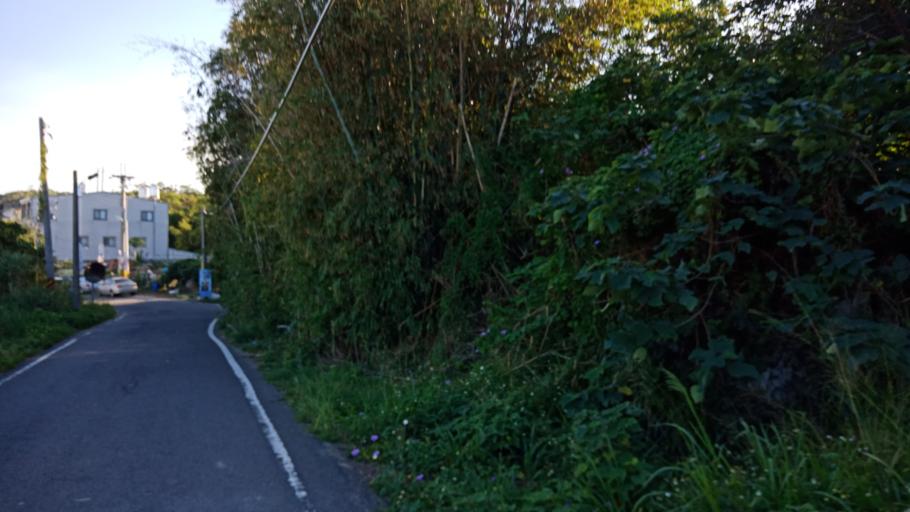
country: TW
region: Taiwan
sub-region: Miaoli
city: Miaoli
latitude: 24.4881
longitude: 120.6949
